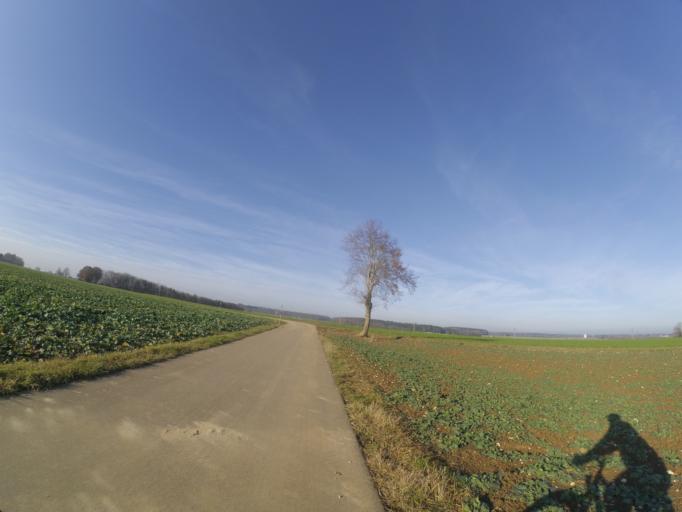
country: DE
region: Baden-Wuerttemberg
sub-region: Tuebingen Region
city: Beimerstetten
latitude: 48.4657
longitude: 9.9685
